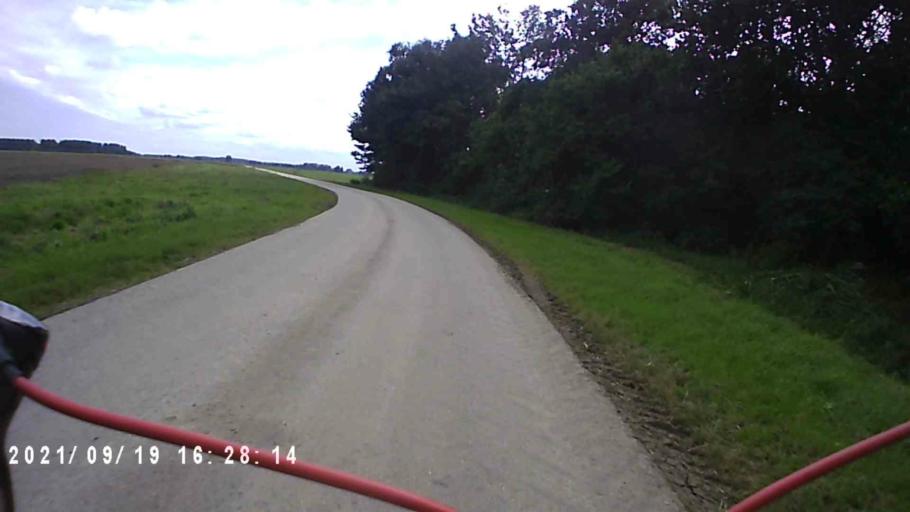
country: DE
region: Lower Saxony
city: Bunde
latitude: 53.1864
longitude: 7.1669
